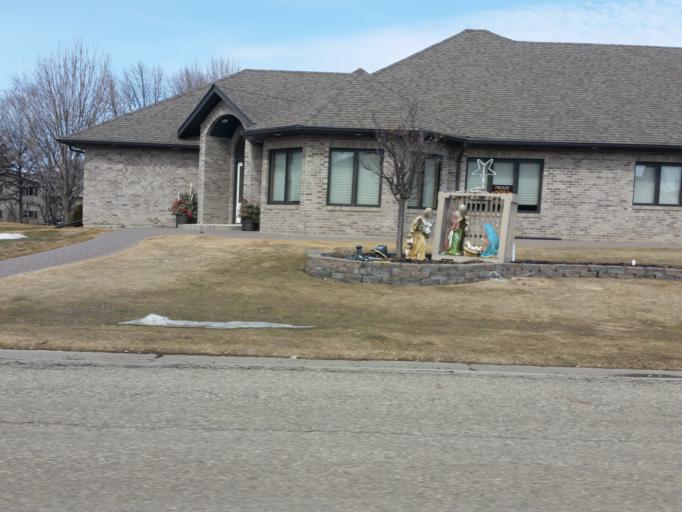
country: US
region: North Dakota
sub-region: Walsh County
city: Grafton
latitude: 48.4047
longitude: -97.4135
